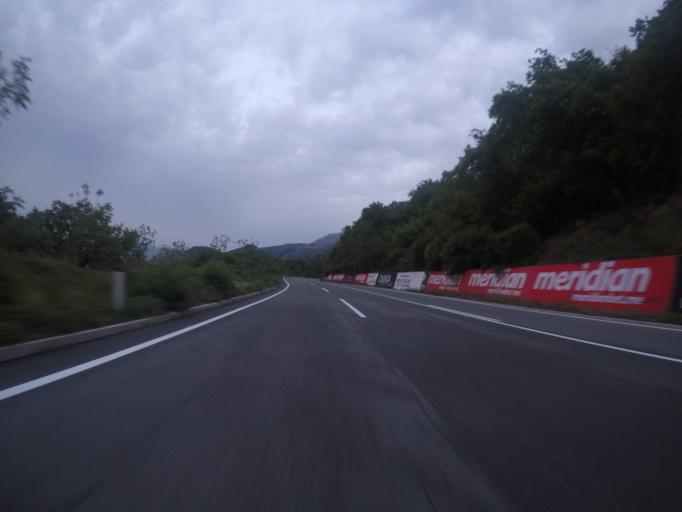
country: ME
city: Petrovac na Moru
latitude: 42.1910
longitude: 18.9870
